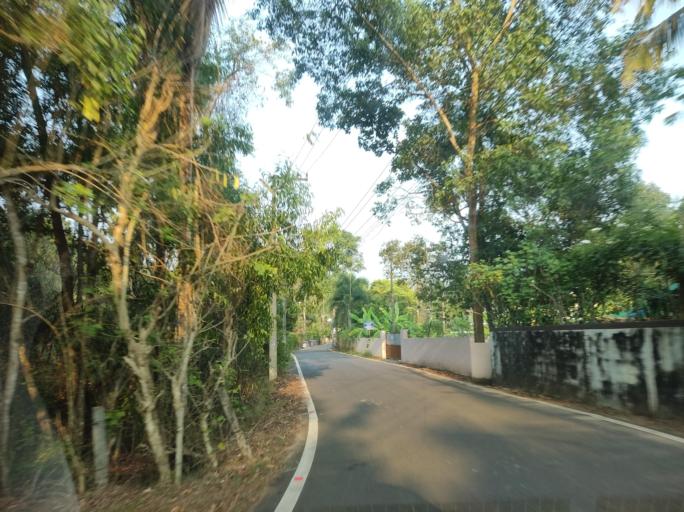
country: IN
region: Kerala
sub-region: Alappuzha
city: Shertallai
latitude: 9.6153
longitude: 76.3139
